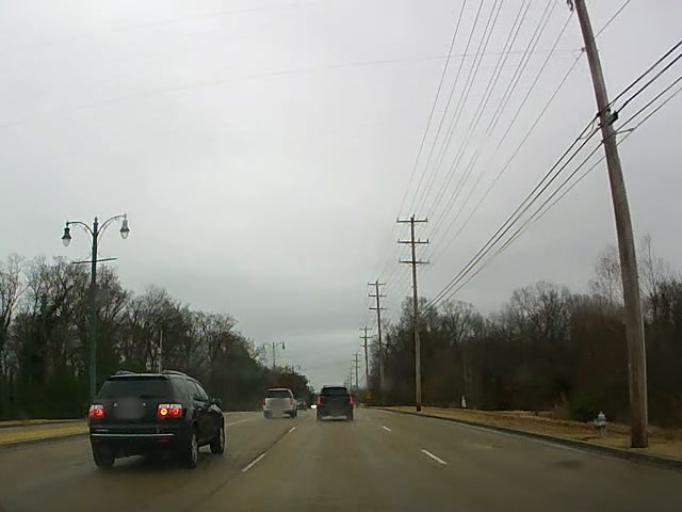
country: US
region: Tennessee
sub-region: Shelby County
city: Germantown
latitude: 35.0474
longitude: -89.7505
